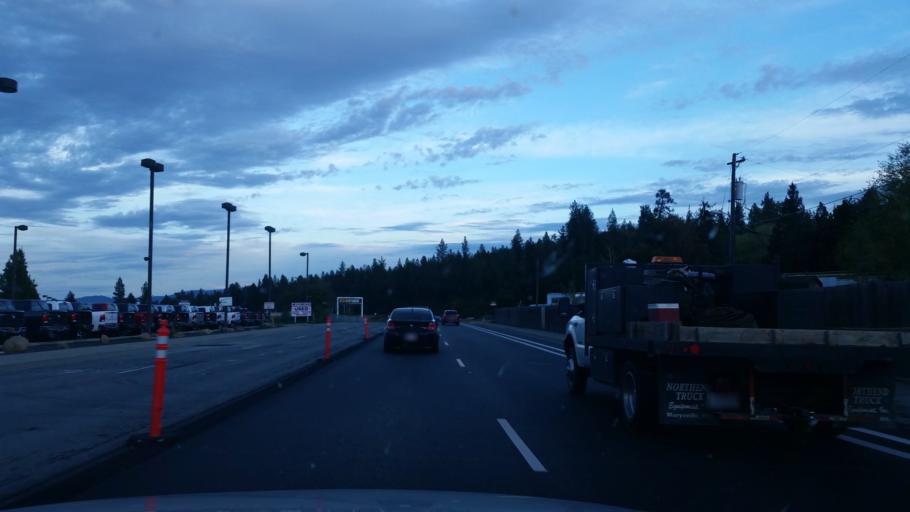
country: US
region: Washington
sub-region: Spokane County
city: Dishman
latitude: 47.6556
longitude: -117.3035
